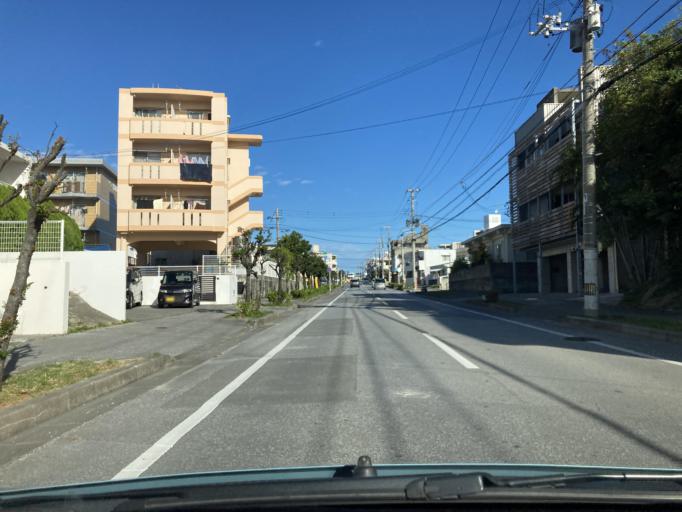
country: JP
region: Okinawa
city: Chatan
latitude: 26.3666
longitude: 127.7475
